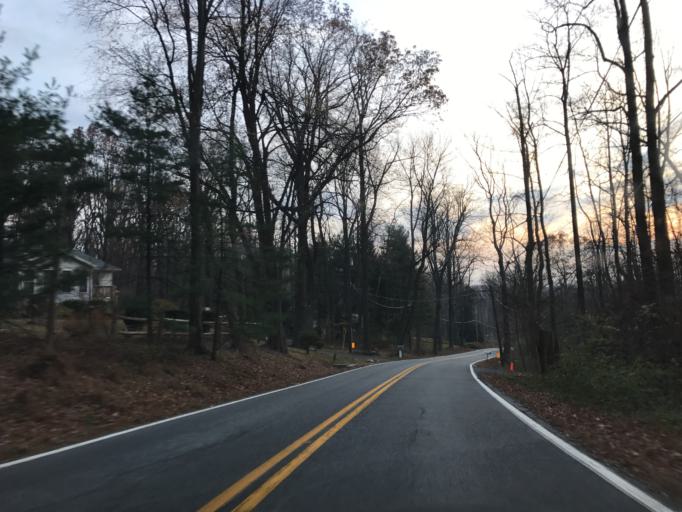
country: US
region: Maryland
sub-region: Frederick County
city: Braddock Heights
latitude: 39.4562
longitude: -77.4919
